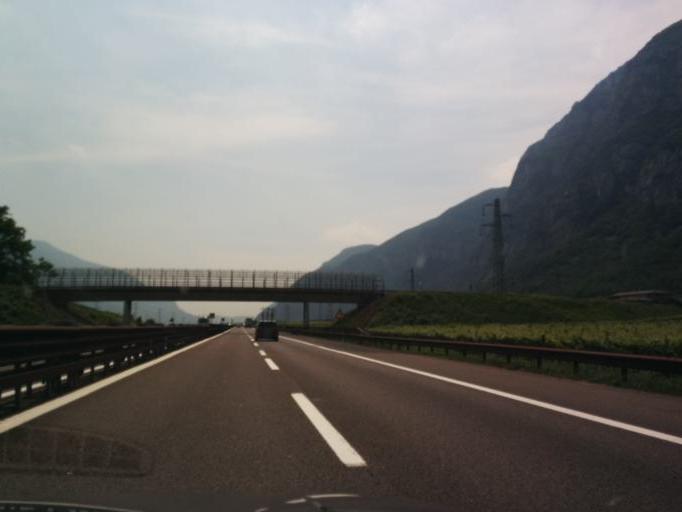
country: IT
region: Veneto
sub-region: Provincia di Verona
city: Rivalta
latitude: 45.6335
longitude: 10.8717
